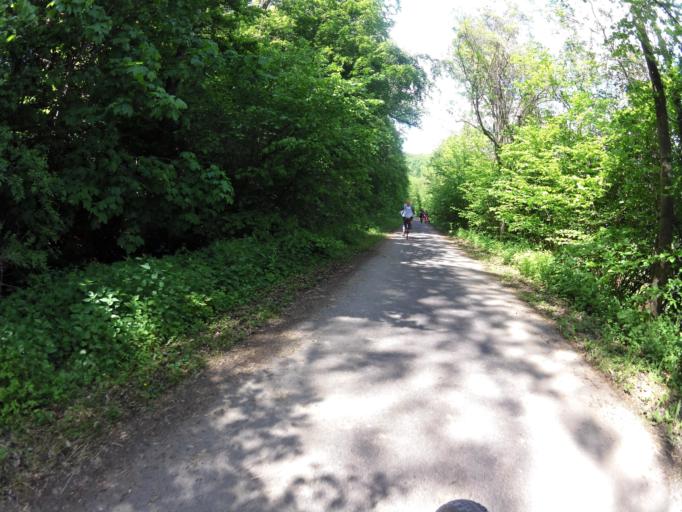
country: DE
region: Thuringia
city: Ebenshausen
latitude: 51.0900
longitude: 10.3022
